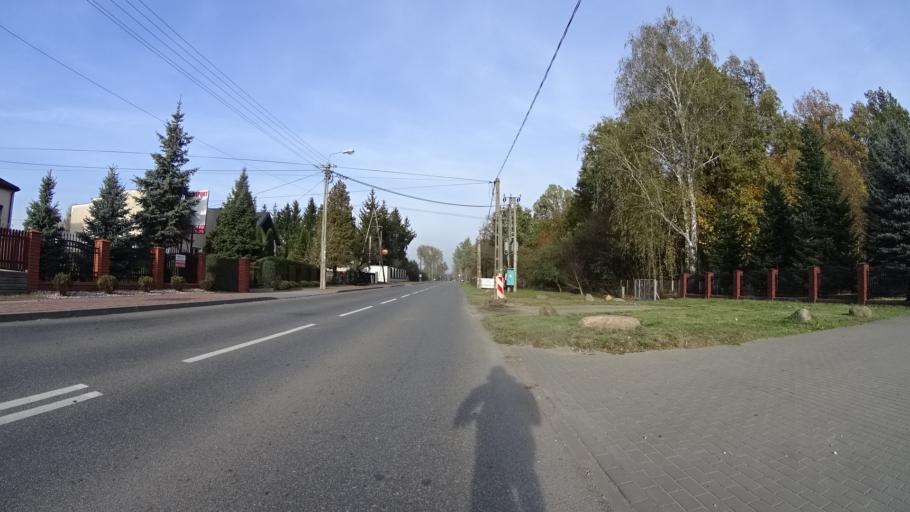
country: PL
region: Masovian Voivodeship
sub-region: Powiat warszawski zachodni
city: Babice
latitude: 52.2545
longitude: 20.8486
